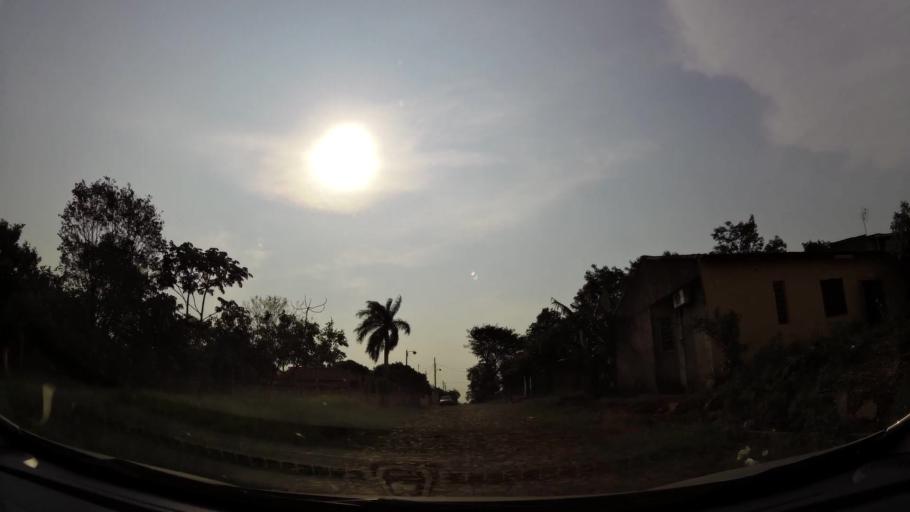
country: PY
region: Alto Parana
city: Ciudad del Este
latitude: -25.4866
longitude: -54.6531
